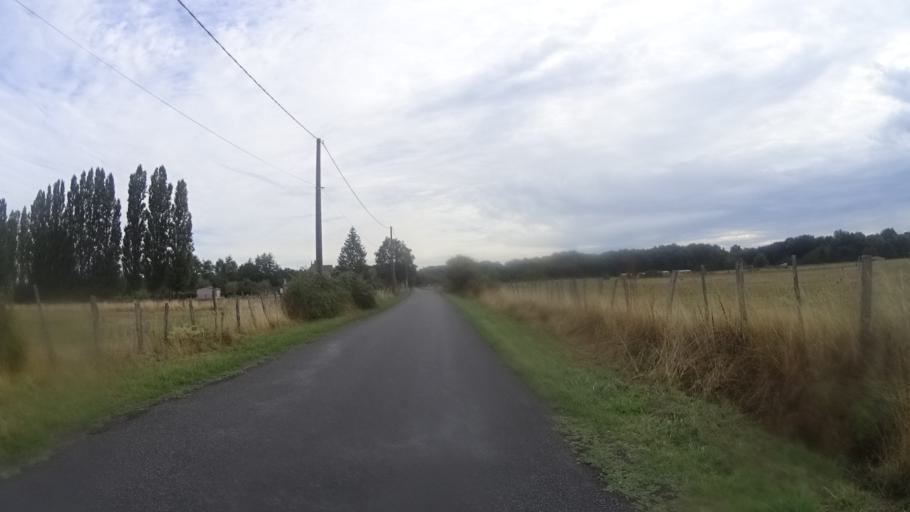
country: FR
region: Centre
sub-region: Departement du Loiret
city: Fay-aux-Loges
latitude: 47.9454
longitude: 2.1660
